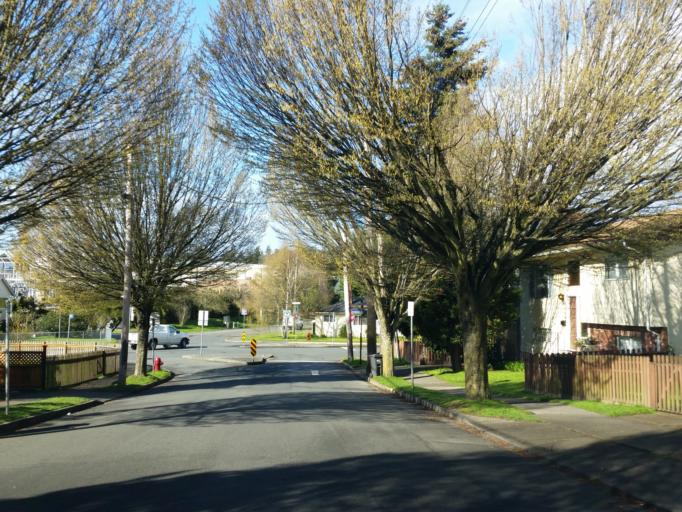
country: CA
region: British Columbia
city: Victoria
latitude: 48.4362
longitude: -123.3931
